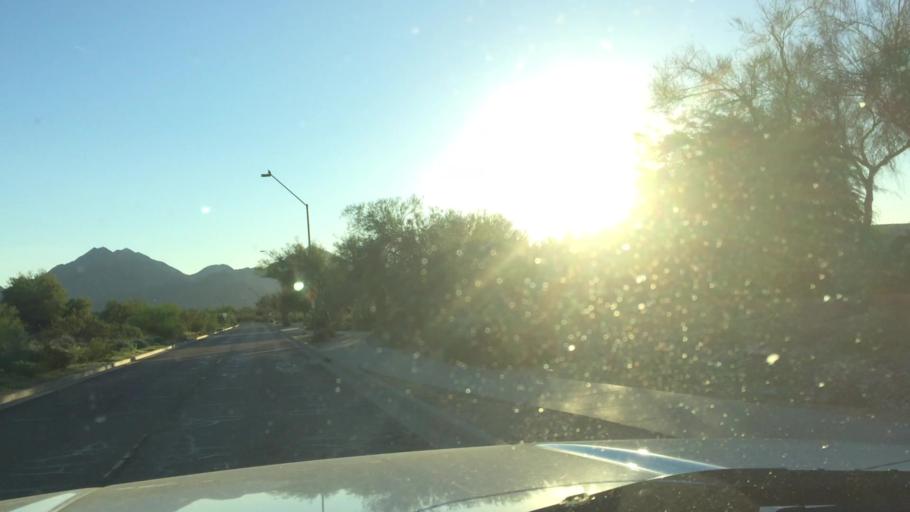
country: US
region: Arizona
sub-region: Maricopa County
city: Paradise Valley
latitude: 33.6494
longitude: -111.9058
